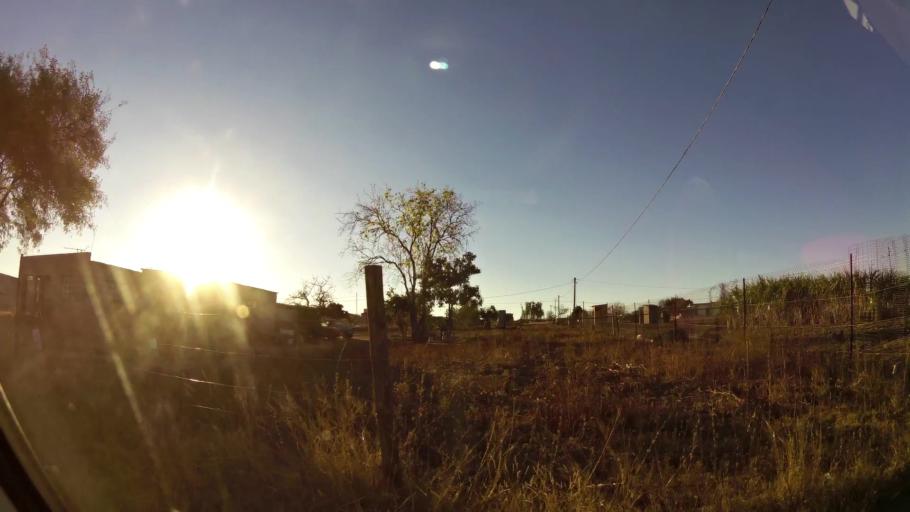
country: ZA
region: Limpopo
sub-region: Capricorn District Municipality
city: Polokwane
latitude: -23.8244
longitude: 29.3782
